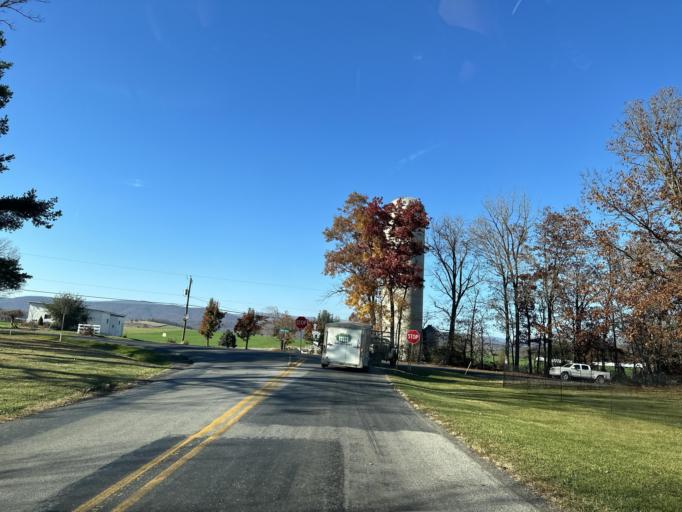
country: US
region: Virginia
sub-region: Rockingham County
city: Bridgewater
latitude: 38.4276
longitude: -79.0435
